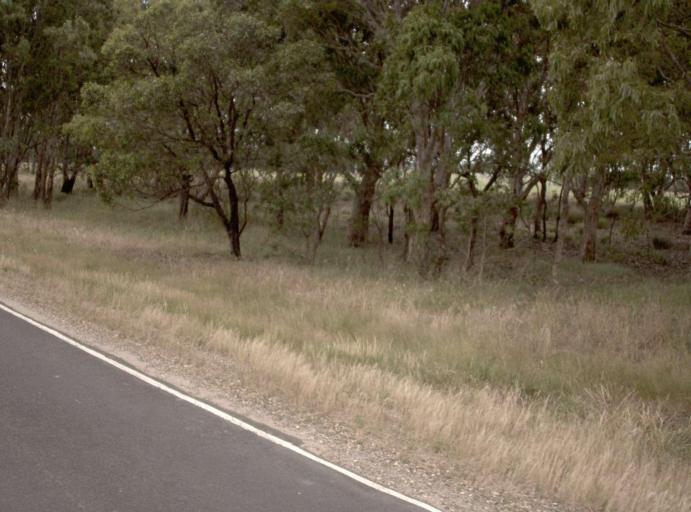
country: AU
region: Victoria
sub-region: Wellington
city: Heyfield
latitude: -38.0412
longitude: 146.7671
